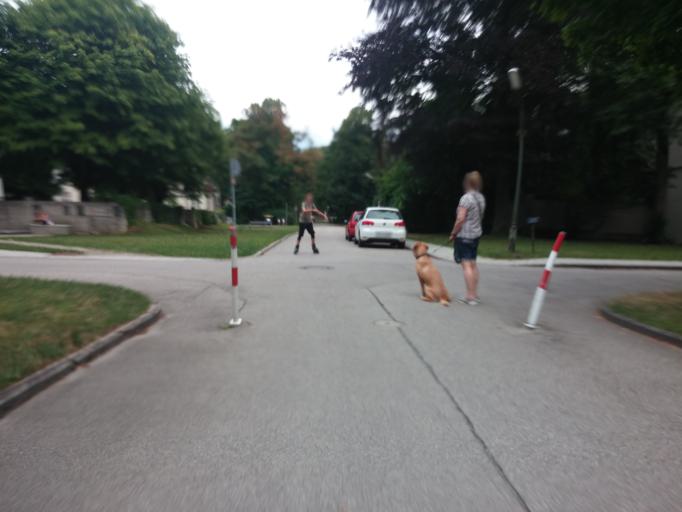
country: DE
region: Bavaria
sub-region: Upper Bavaria
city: Haar
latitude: 48.1133
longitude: 11.7399
